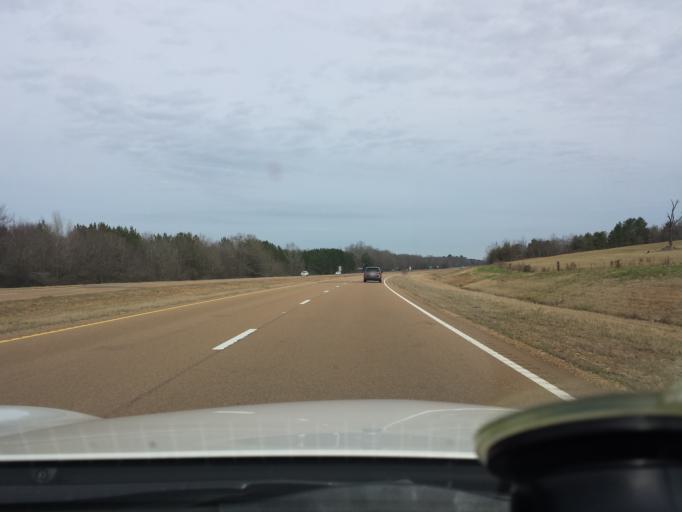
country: US
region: Mississippi
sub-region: Leake County
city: Carthage
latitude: 32.6573
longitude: -89.6508
